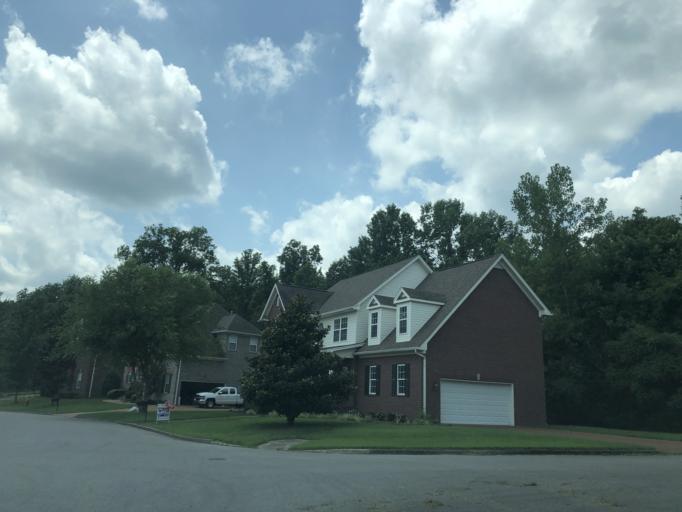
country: US
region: Tennessee
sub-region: Williamson County
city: Brentwood Estates
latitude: 36.0180
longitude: -86.7174
